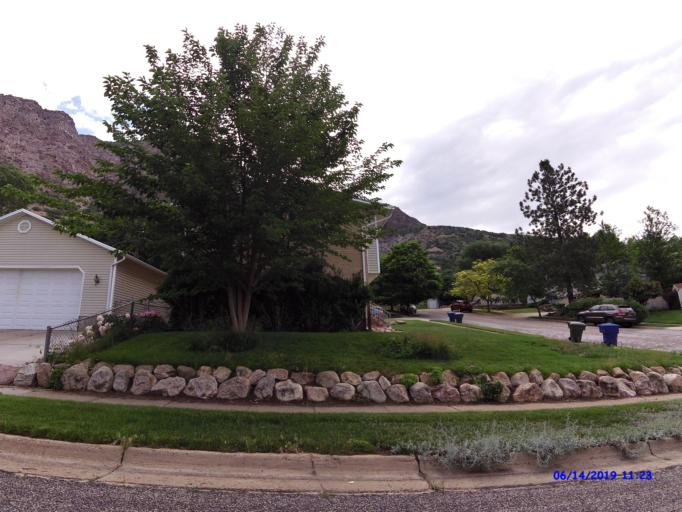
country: US
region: Utah
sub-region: Weber County
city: Ogden
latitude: 41.2578
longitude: -111.9398
